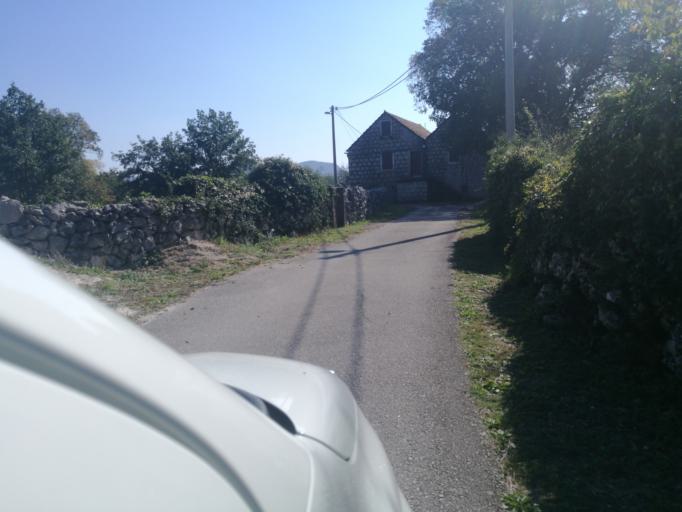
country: HR
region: Splitsko-Dalmatinska
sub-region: Grad Omis
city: Omis
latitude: 43.5205
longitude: 16.7485
